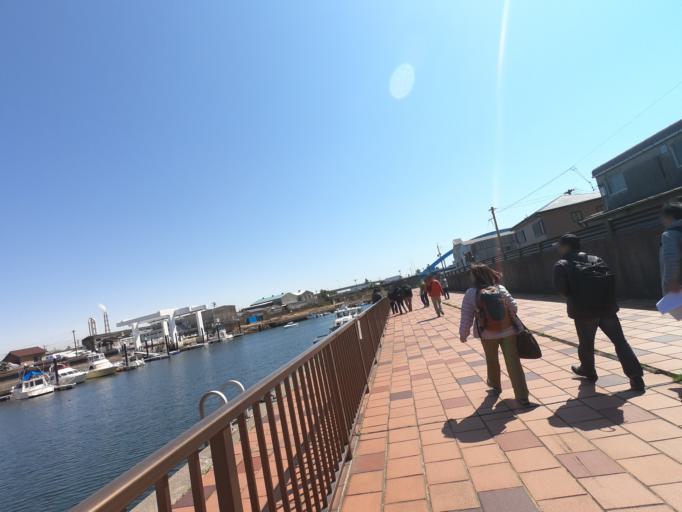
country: JP
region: Mie
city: Yokkaichi
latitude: 35.0079
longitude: 136.6648
